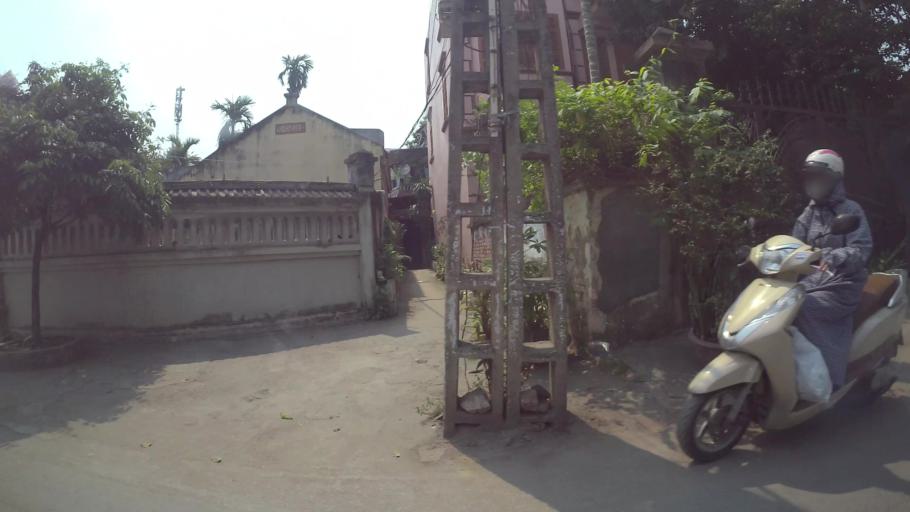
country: VN
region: Ha Noi
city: Thanh Xuan
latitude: 21.0031
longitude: 105.8110
